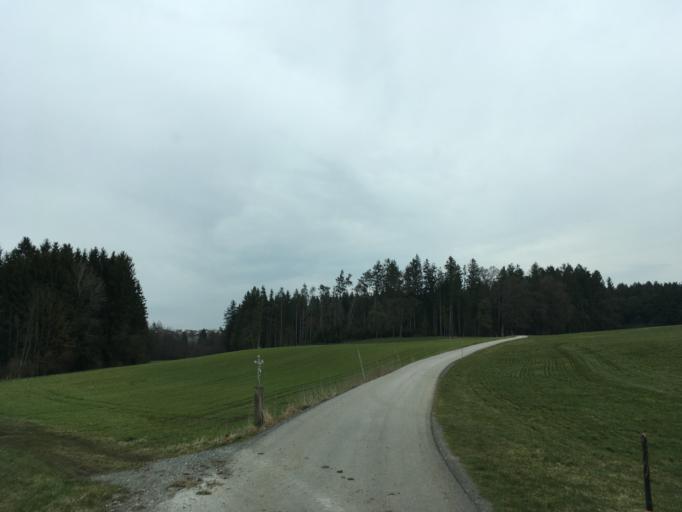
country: DE
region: Bavaria
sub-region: Upper Bavaria
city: Schnaitsee
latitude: 48.0573
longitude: 12.3740
